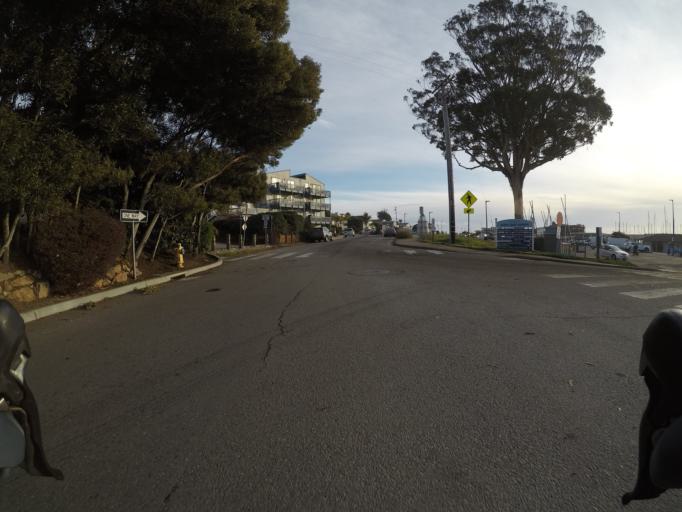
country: US
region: California
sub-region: Santa Cruz County
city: Twin Lakes
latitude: 36.9655
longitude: -122.0007
